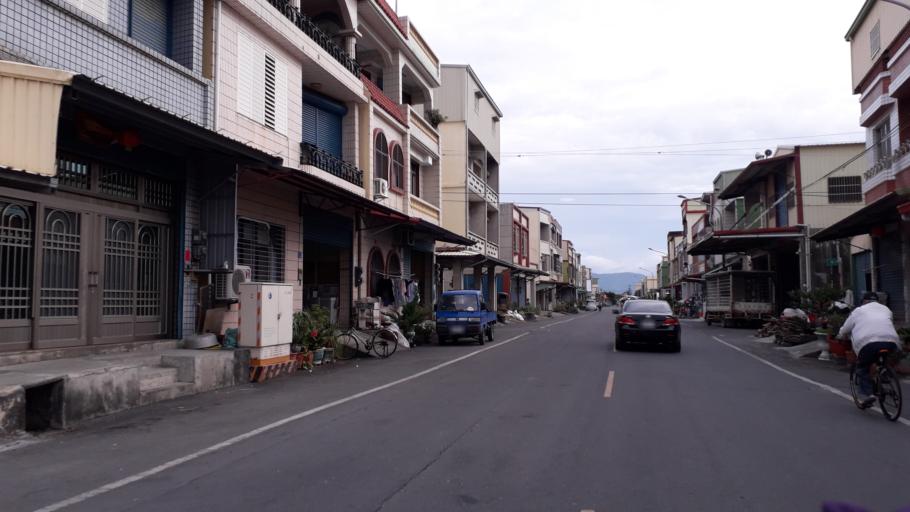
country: TW
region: Taiwan
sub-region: Pingtung
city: Pingtung
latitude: 22.3593
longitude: 120.5978
